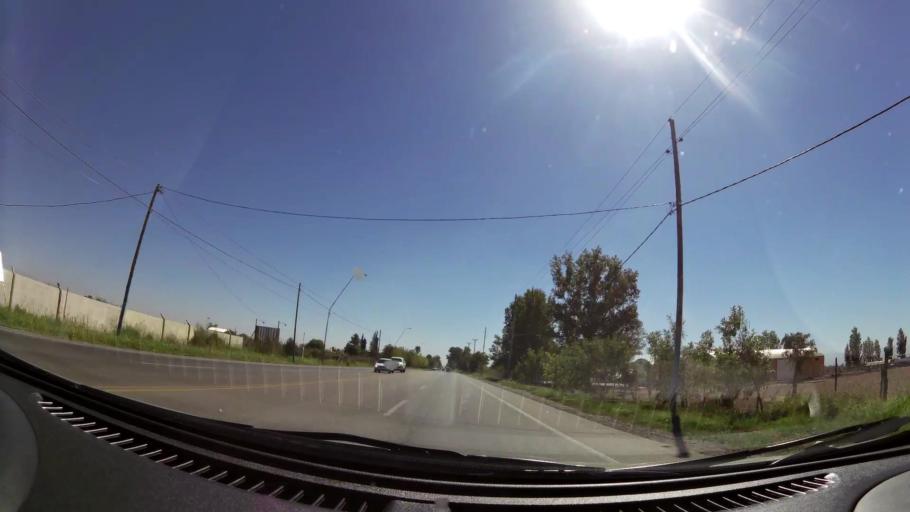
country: AR
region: San Juan
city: Villa Aberastain
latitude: -31.6215
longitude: -68.5507
